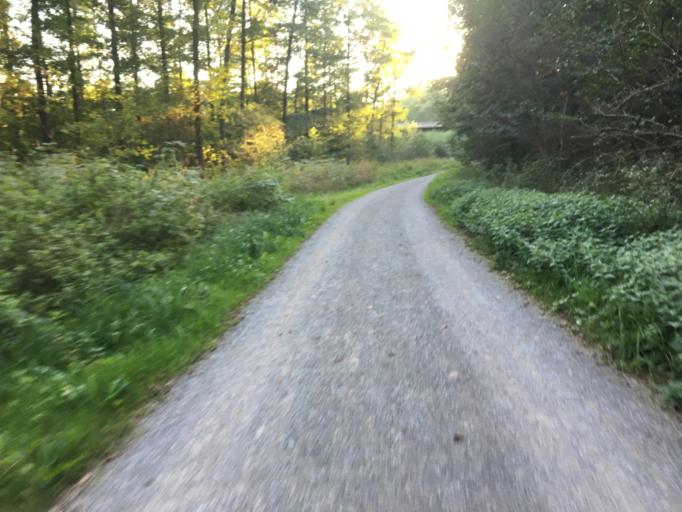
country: DE
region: Baden-Wuerttemberg
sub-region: Regierungsbezirk Stuttgart
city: Boeblingen
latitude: 48.6635
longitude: 8.9925
